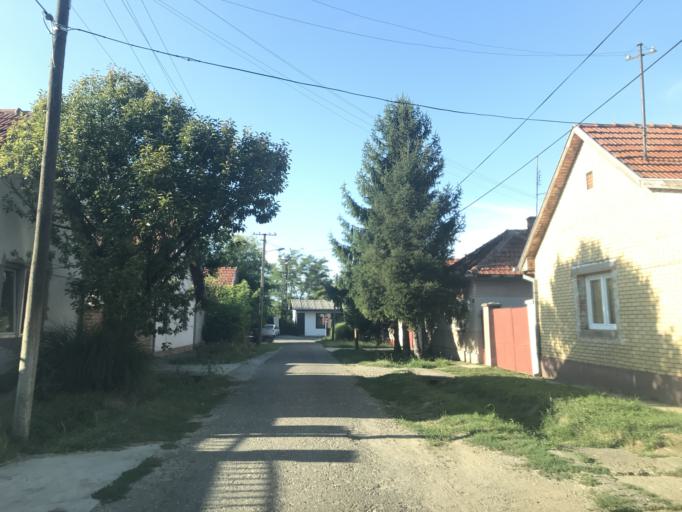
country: RS
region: Autonomna Pokrajina Vojvodina
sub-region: Juznobacki Okrug
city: Novi Sad
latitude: 45.2131
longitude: 19.8036
